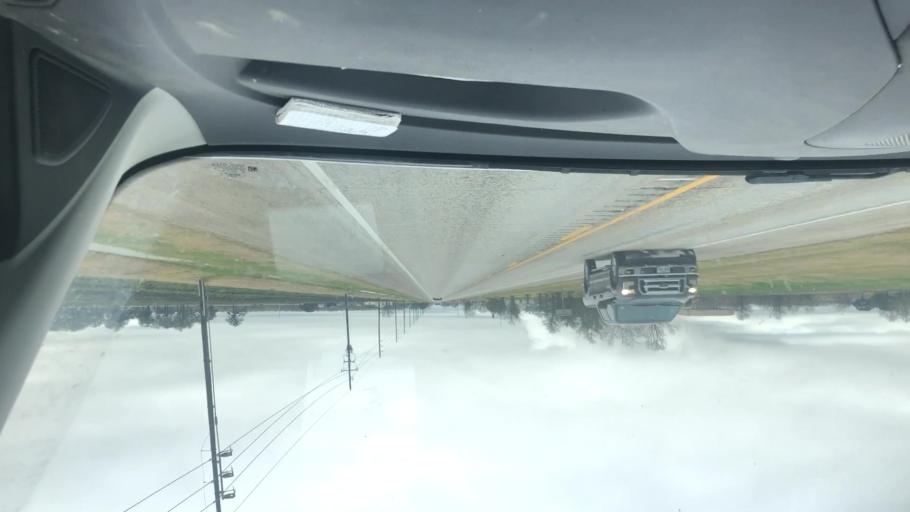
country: US
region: Texas
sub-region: Wharton County
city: Wharton
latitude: 29.3022
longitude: -96.0792
